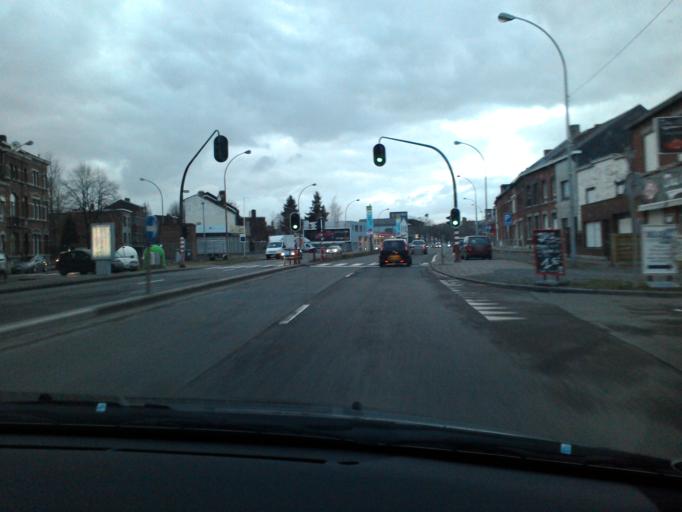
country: BE
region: Wallonia
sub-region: Province de Liege
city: Liege
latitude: 50.6188
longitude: 5.5956
